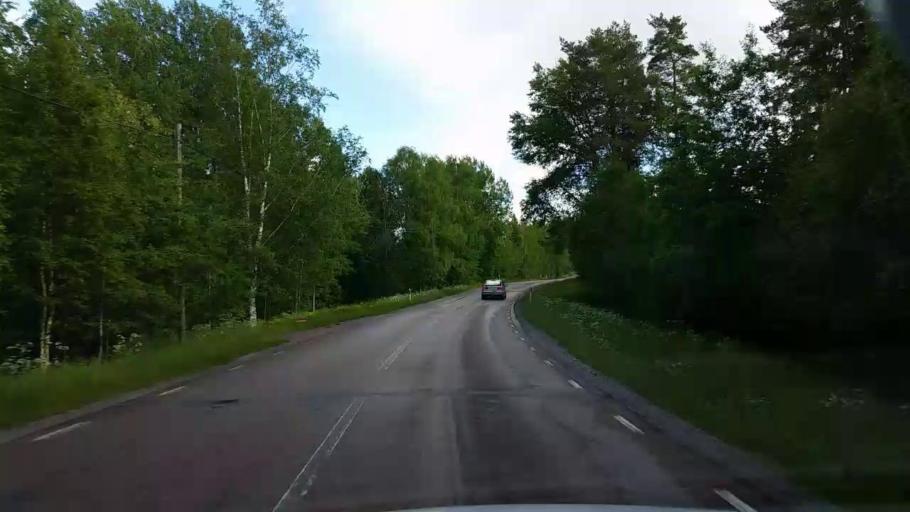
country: SE
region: Vaestmanland
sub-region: Fagersta Kommun
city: Fagersta
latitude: 59.9348
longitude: 15.8242
